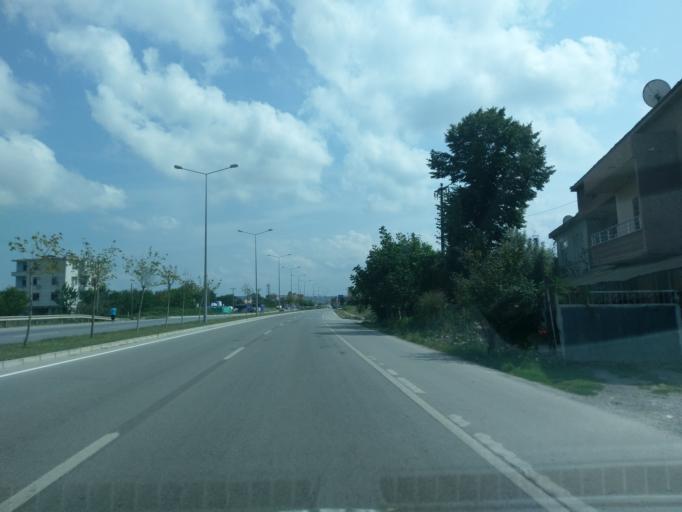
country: TR
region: Samsun
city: Bafra
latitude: 41.5719
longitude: 35.8709
